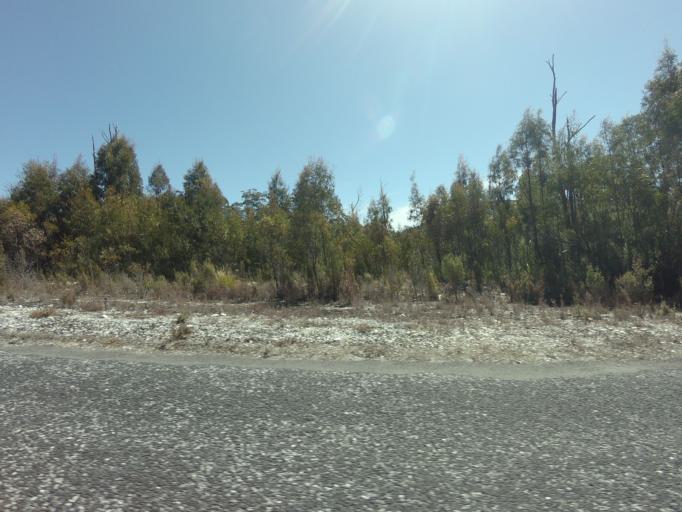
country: AU
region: Tasmania
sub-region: West Coast
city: Queenstown
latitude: -42.8043
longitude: 146.0954
